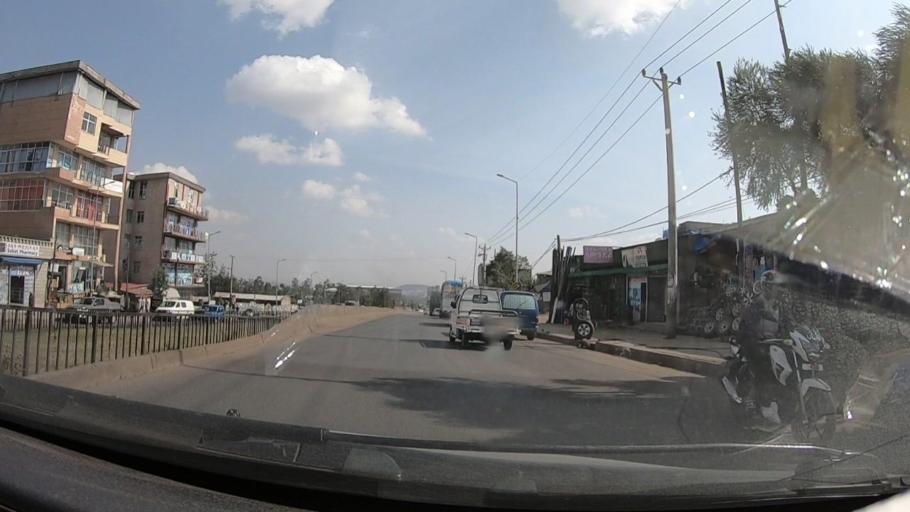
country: ET
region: Adis Abeba
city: Addis Ababa
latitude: 8.9882
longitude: 38.6925
